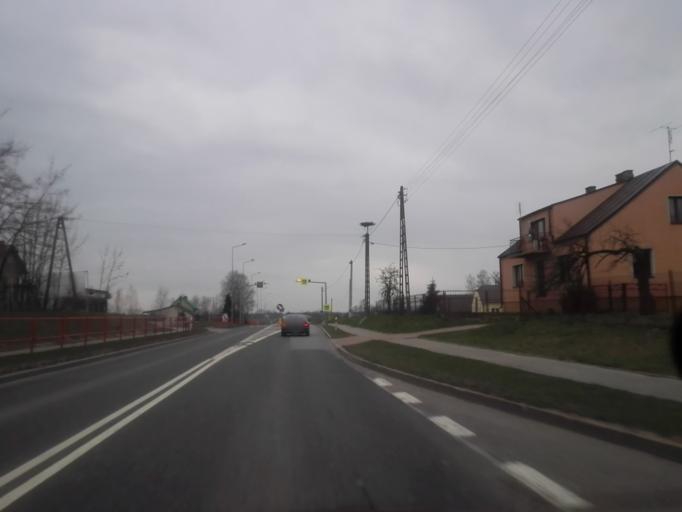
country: PL
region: Podlasie
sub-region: Powiat grajewski
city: Grajewo
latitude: 53.6720
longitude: 22.5682
